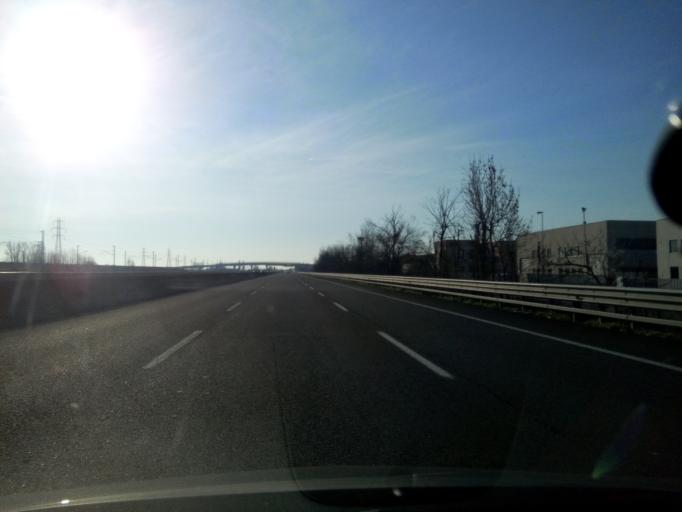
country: IT
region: Emilia-Romagna
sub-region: Provincia di Reggio Emilia
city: Praticello
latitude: 44.7951
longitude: 10.4622
